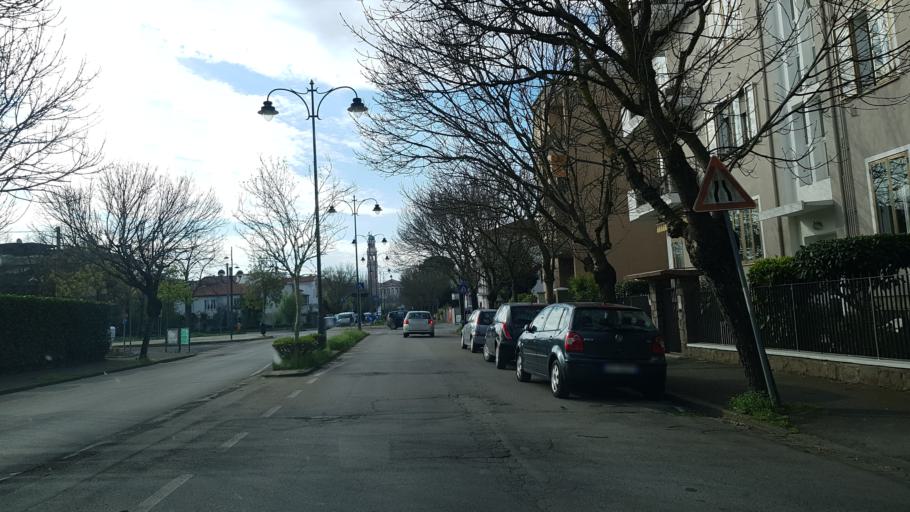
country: IT
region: Veneto
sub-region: Provincia di Rovigo
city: Rovigo
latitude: 45.0774
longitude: 11.7913
